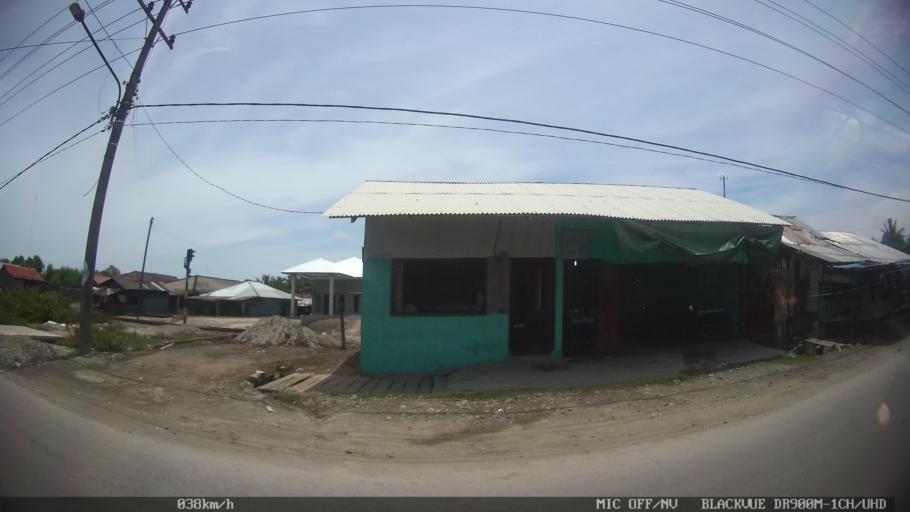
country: ID
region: North Sumatra
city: Belawan
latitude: 3.7628
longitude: 98.6820
